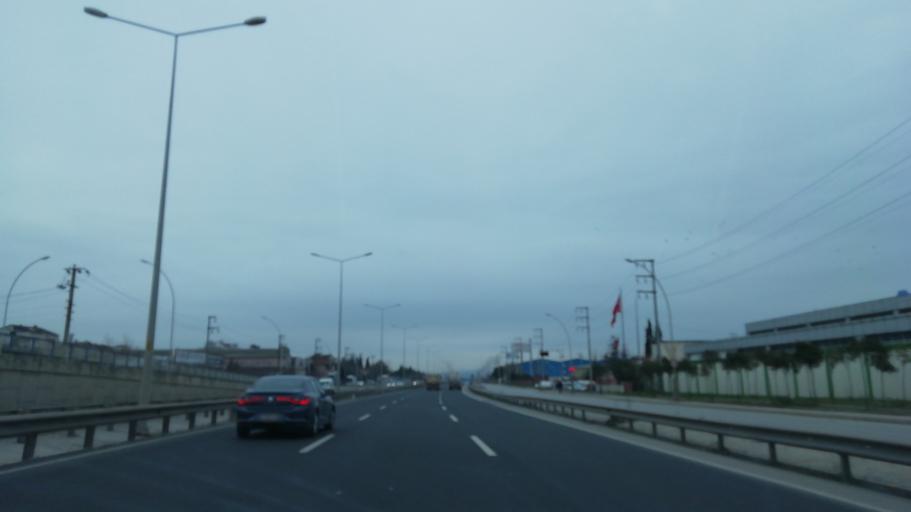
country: TR
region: Kocaeli
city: Gebze
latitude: 40.7984
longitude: 29.4453
